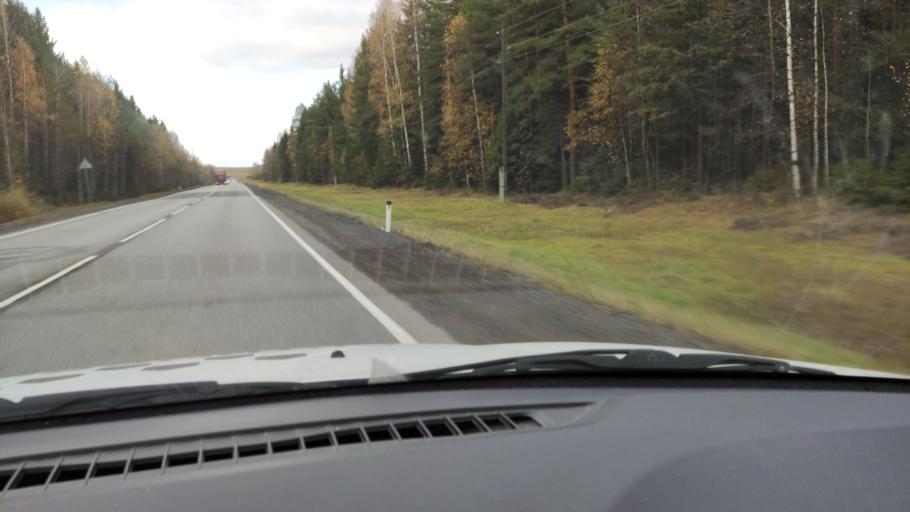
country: RU
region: Kirov
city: Belaya Kholunitsa
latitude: 58.8826
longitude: 50.8726
